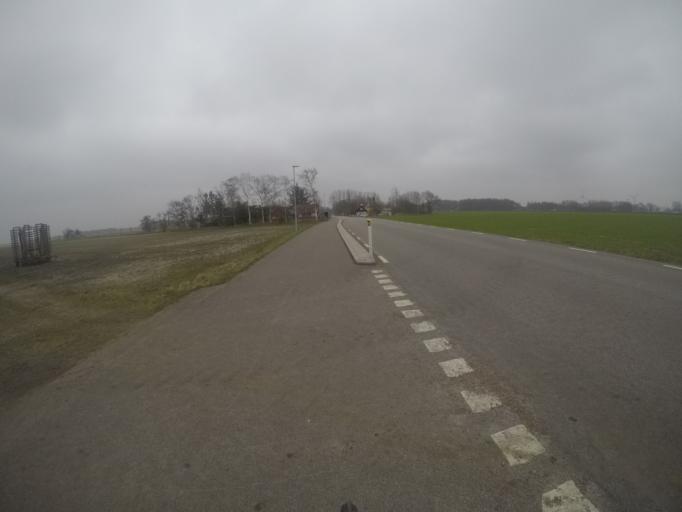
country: SE
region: Skane
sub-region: Helsingborg
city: Odakra
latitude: 56.2172
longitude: 12.6845
